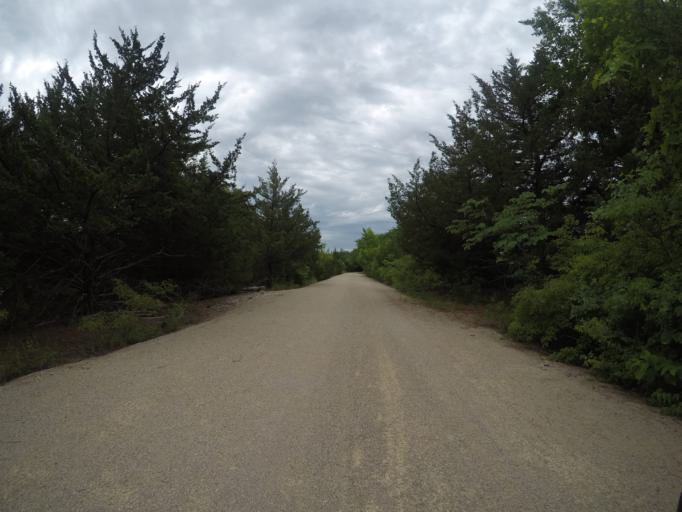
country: US
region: Kansas
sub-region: Anderson County
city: Garnett
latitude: 38.3070
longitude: -95.2463
